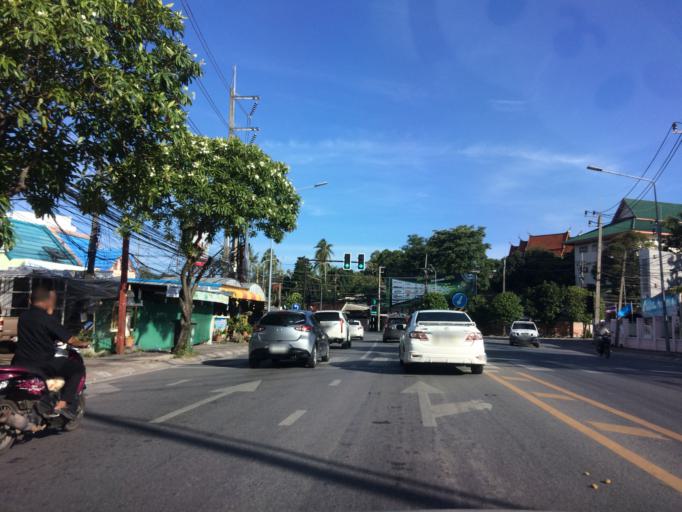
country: TH
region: Phuket
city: Kathu
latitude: 7.9007
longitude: 98.3531
